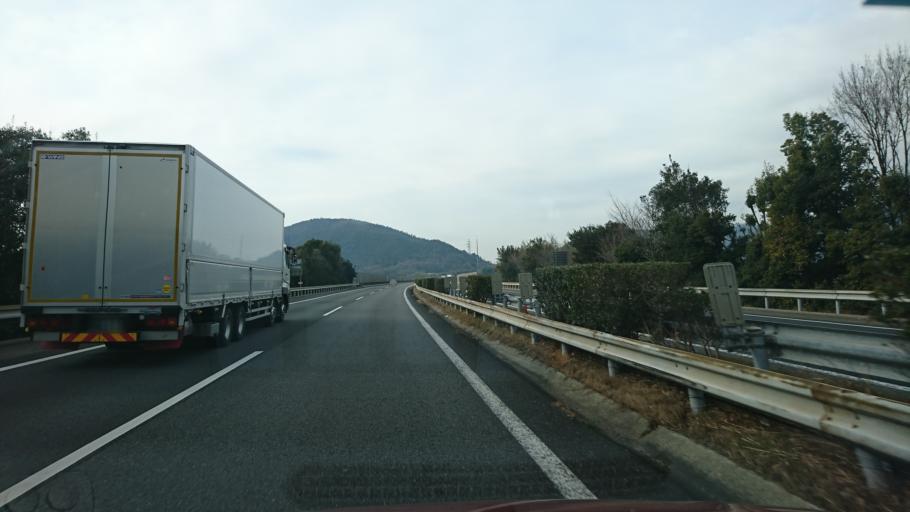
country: JP
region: Okayama
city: Kamogatacho-kamogata
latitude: 34.5386
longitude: 133.5628
